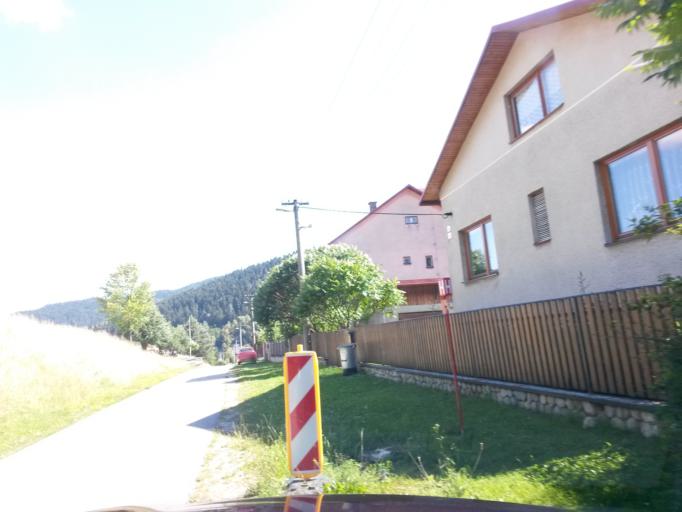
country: SK
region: Kosicky
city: Spisska Nova Ves
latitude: 48.8435
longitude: 20.6217
